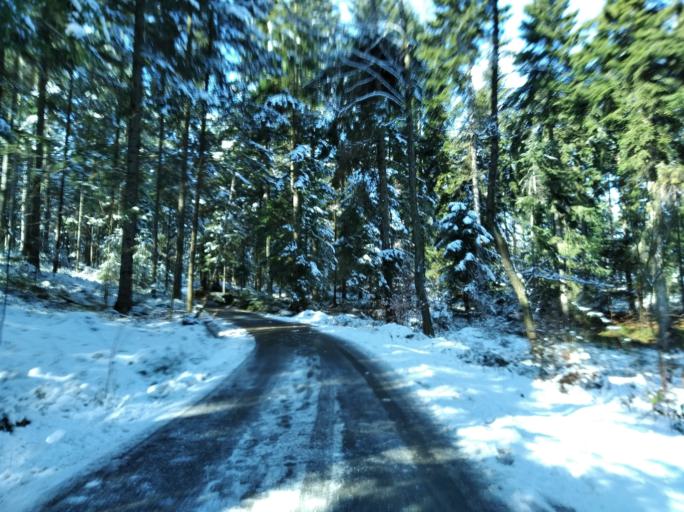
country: PL
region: Subcarpathian Voivodeship
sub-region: Powiat krosnienski
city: Korczyna
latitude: 49.7422
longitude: 21.8285
